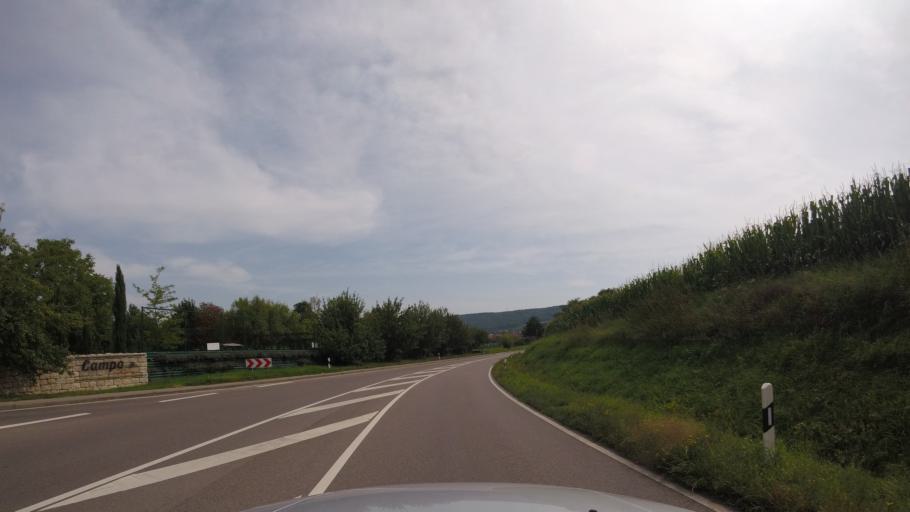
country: DE
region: Baden-Wuerttemberg
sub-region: Regierungsbezirk Stuttgart
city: Grossbottwar
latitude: 49.0036
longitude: 9.2842
